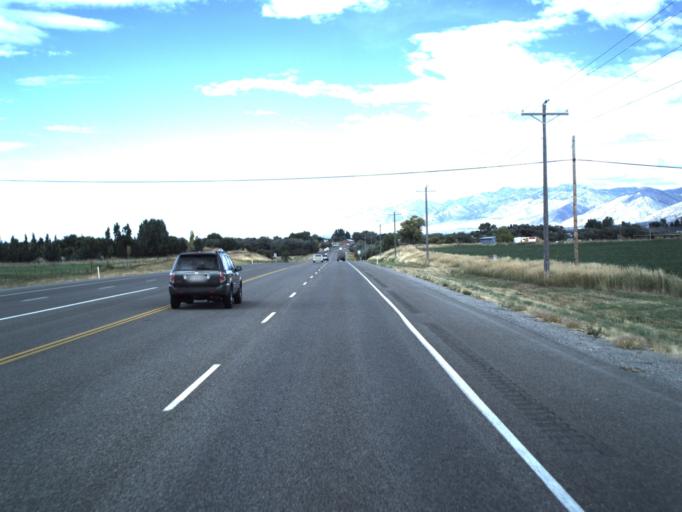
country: US
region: Utah
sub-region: Cache County
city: Wellsville
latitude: 41.6345
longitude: -111.9208
